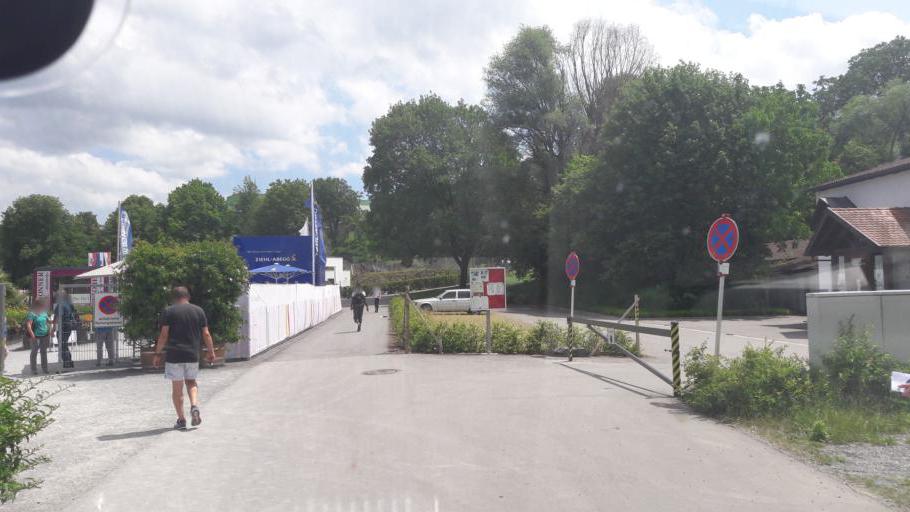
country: DE
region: Baden-Wuerttemberg
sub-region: Regierungsbezirk Stuttgart
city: Ohringen
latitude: 49.1966
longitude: 9.5109
